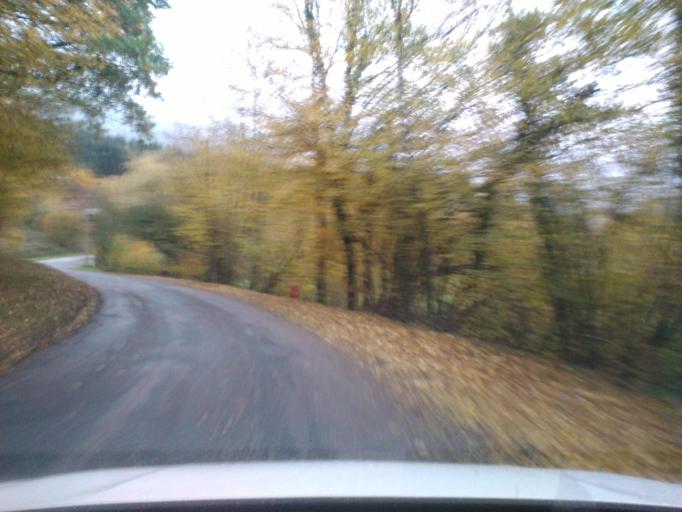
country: FR
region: Lorraine
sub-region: Departement des Vosges
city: Sainte-Marguerite
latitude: 48.2891
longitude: 7.0044
